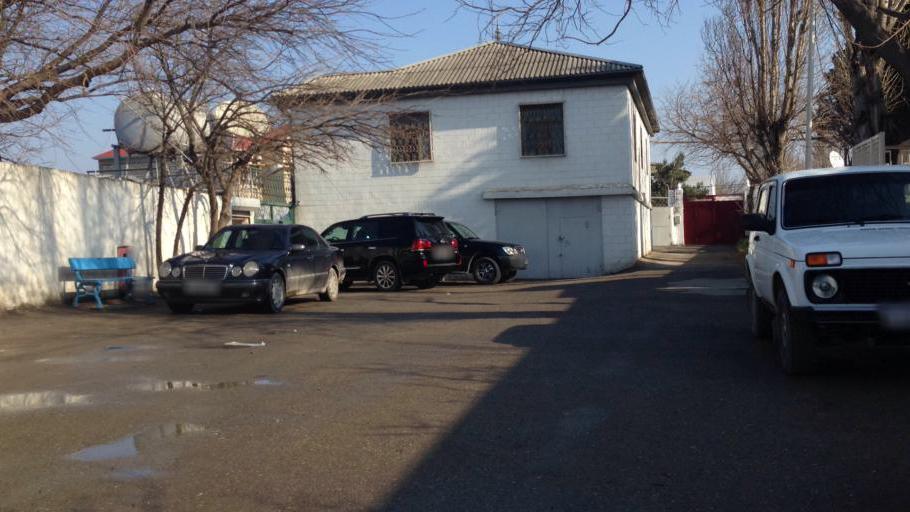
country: AZ
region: Baki
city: Binagadi
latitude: 40.4362
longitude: 49.8533
